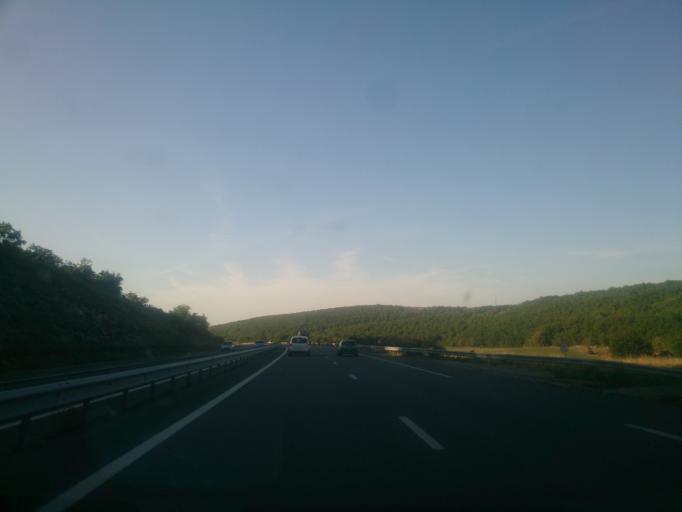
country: FR
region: Midi-Pyrenees
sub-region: Departement du Lot
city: Le Vigan
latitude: 44.7660
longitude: 1.5399
